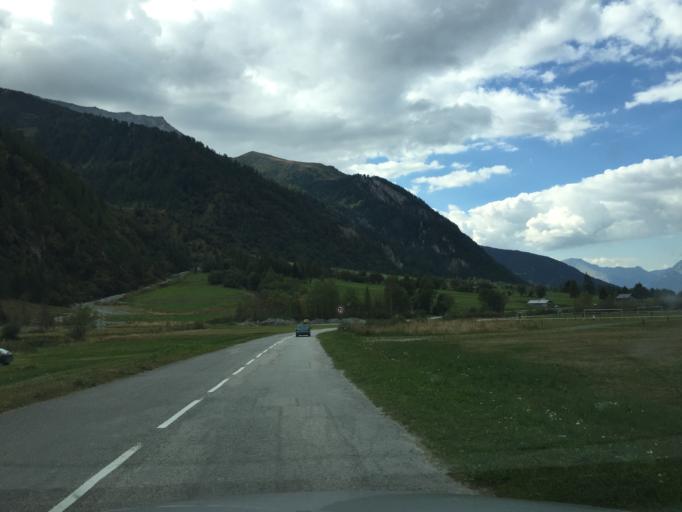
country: FR
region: Rhone-Alpes
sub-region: Departement de la Savoie
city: Belle-Plagne
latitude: 45.5186
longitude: 6.8020
